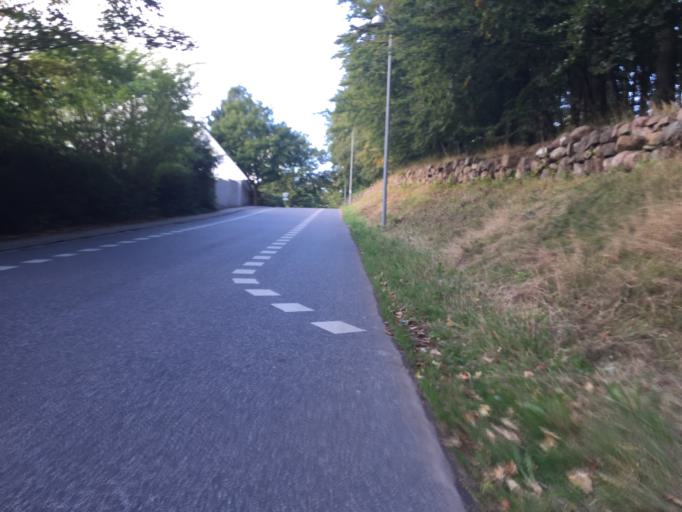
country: DK
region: Capital Region
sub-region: Herlev Kommune
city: Herlev
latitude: 55.7600
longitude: 12.4129
